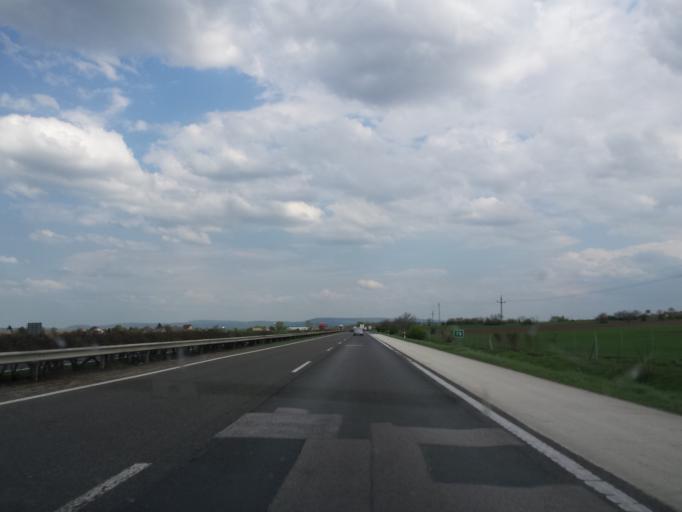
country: HU
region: Komarom-Esztergom
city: Mocsa
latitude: 47.6620
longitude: 18.1675
